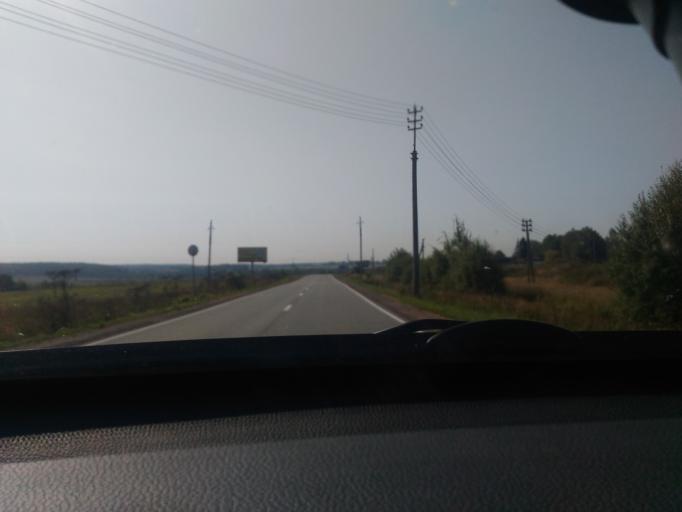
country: RU
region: Moskovskaya
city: Podosinki
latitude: 56.2375
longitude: 37.5493
